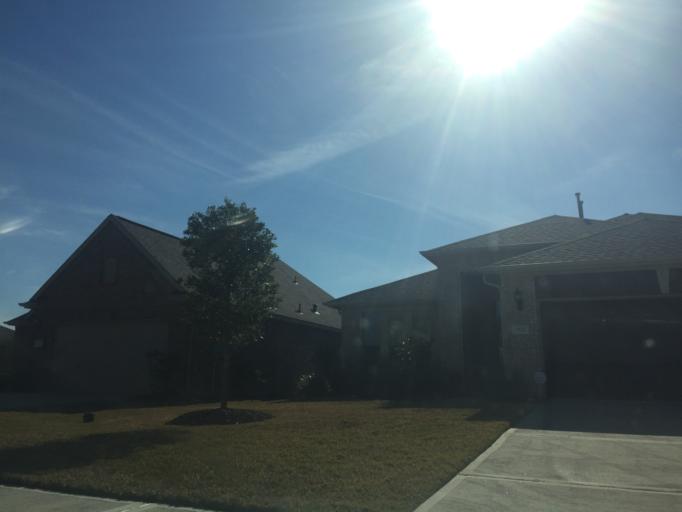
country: US
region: Texas
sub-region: Galveston County
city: Bacliff
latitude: 29.5100
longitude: -95.0107
